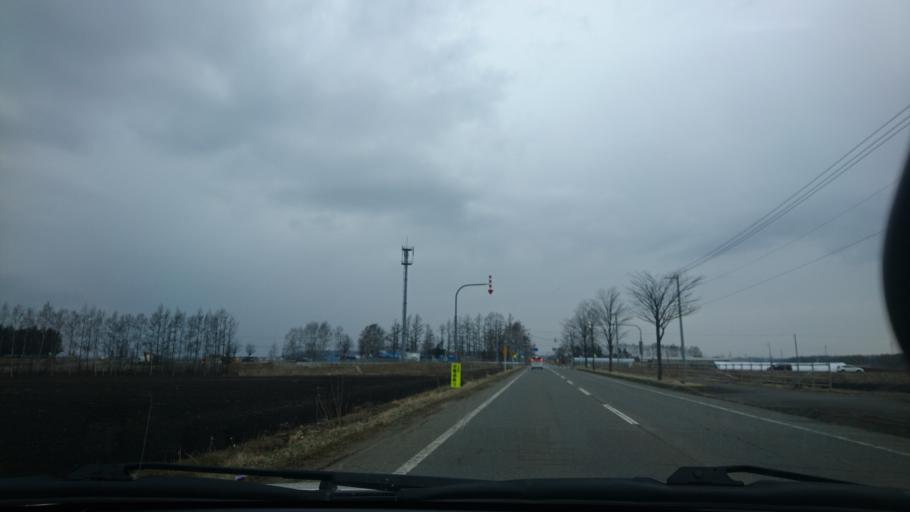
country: JP
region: Hokkaido
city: Otofuke
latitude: 42.9710
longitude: 143.1876
